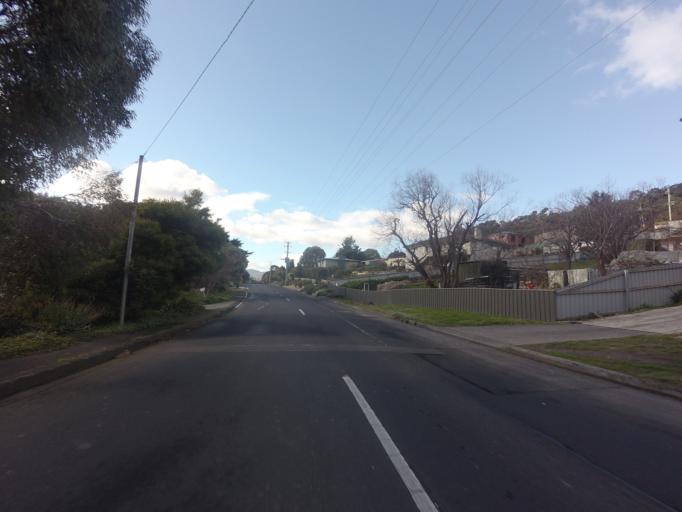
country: AU
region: Tasmania
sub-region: Glenorchy
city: Berriedale
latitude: -42.8173
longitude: 147.2244
